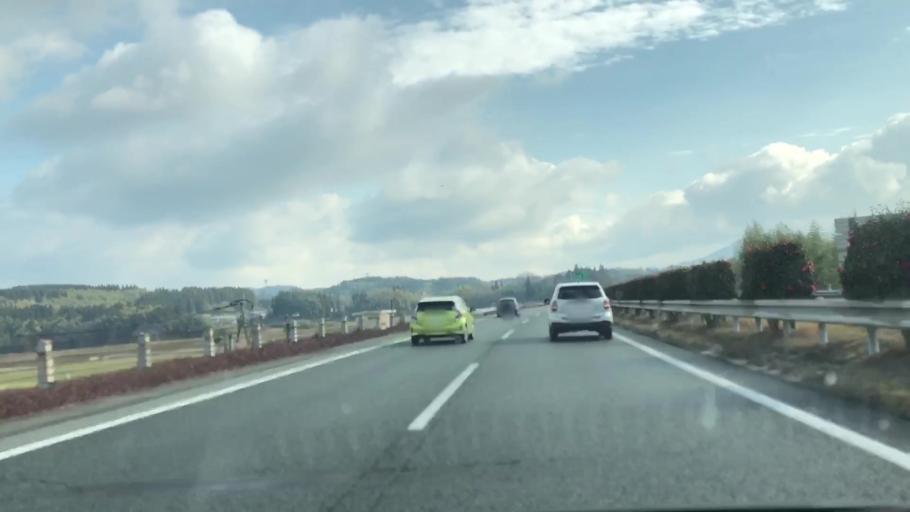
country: JP
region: Kumamoto
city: Tamana
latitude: 32.9948
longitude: 130.5993
